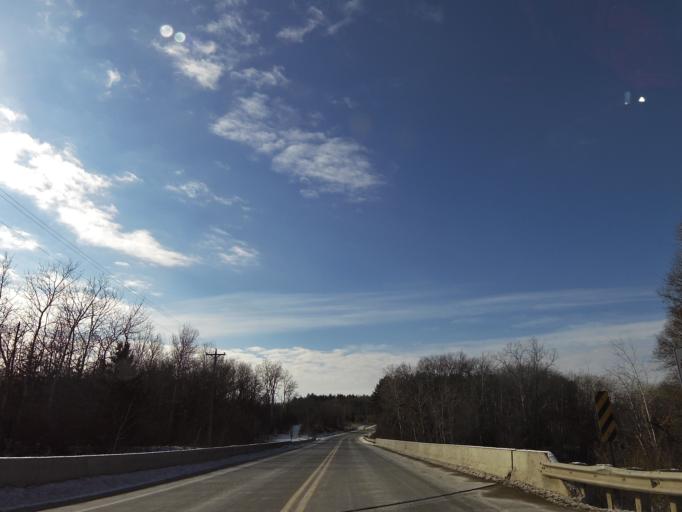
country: US
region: Wisconsin
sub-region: Saint Croix County
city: Roberts
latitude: 44.9916
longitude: -92.6165
